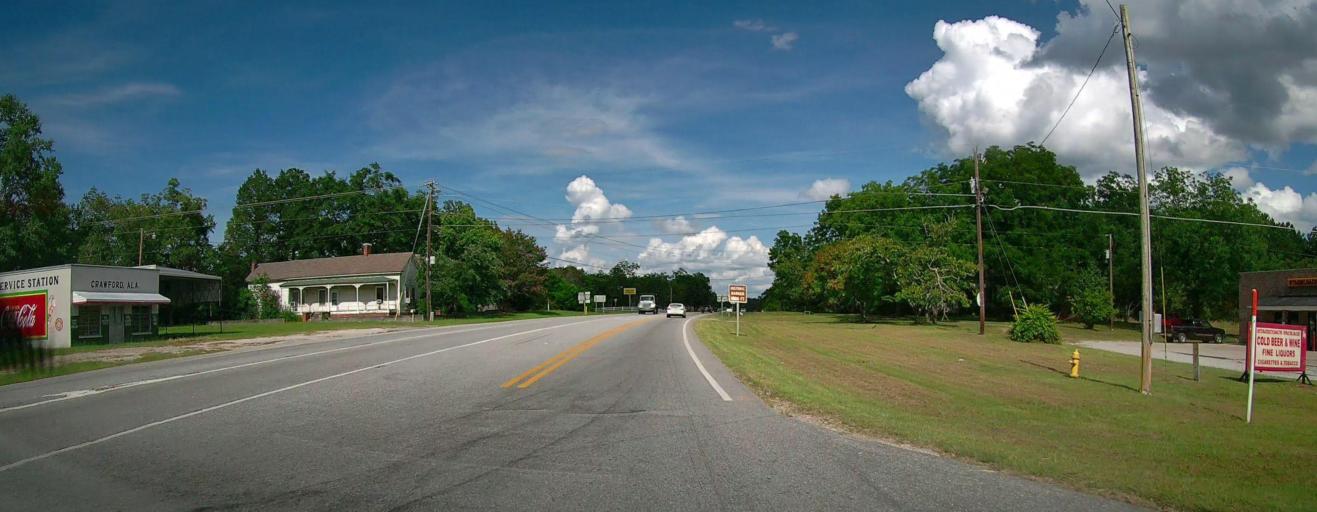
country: US
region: Alabama
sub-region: Russell County
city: Ladonia
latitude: 32.4563
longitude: -85.1960
